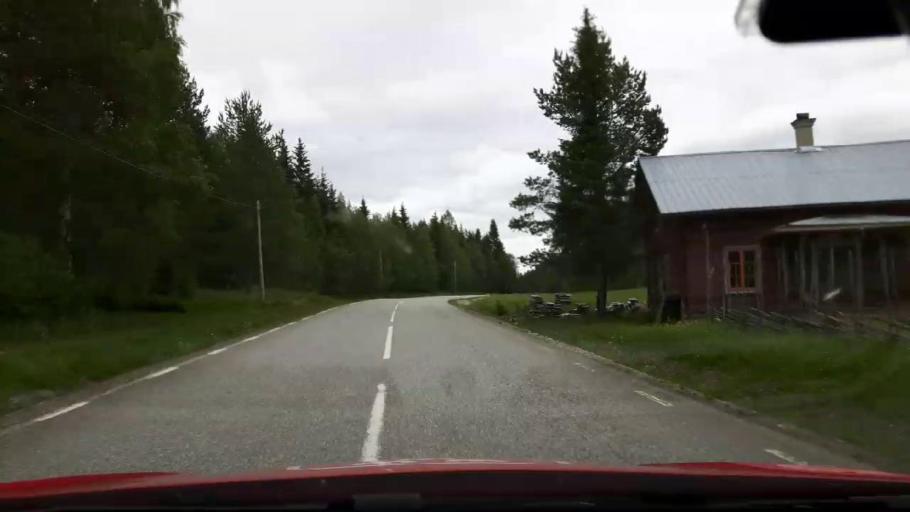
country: SE
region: Jaemtland
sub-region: Ragunda Kommun
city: Hammarstrand
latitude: 63.2429
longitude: 15.9133
